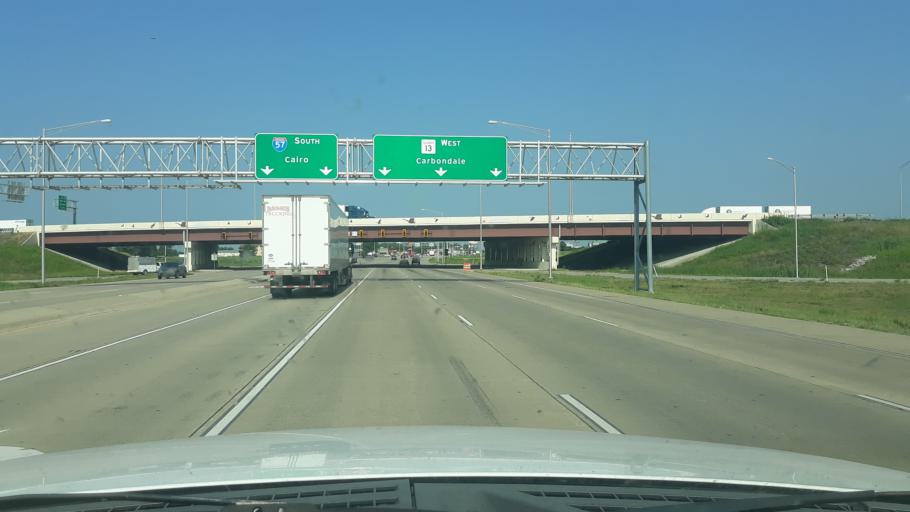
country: US
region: Illinois
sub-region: Williamson County
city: Marion
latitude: 37.7407
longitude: -88.9562
